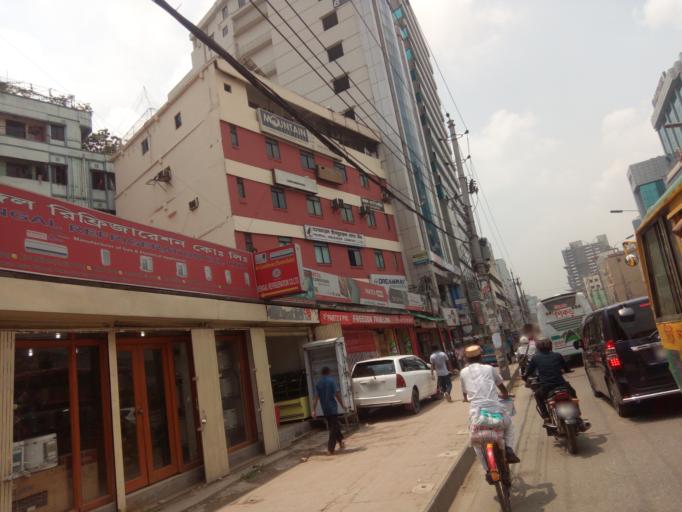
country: BD
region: Dhaka
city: Azimpur
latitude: 23.7552
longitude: 90.3913
